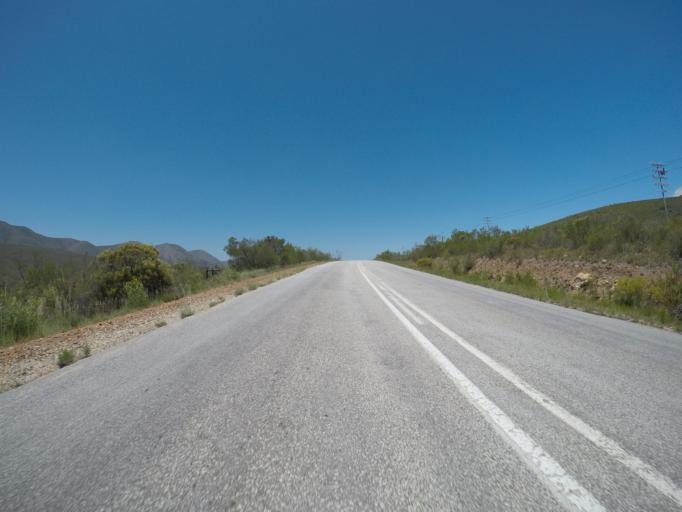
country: ZA
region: Eastern Cape
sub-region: Cacadu District Municipality
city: Kareedouw
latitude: -33.8858
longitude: 24.0820
